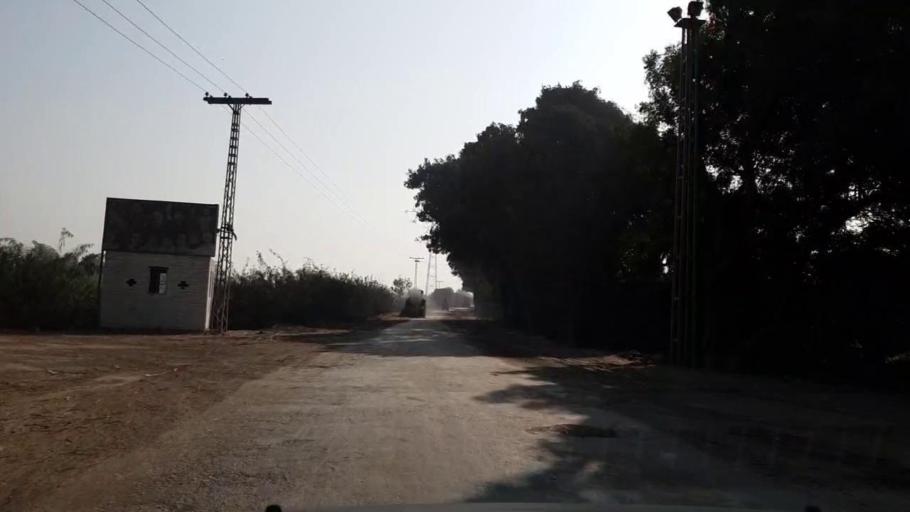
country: PK
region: Sindh
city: Matiari
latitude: 25.5801
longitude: 68.4979
